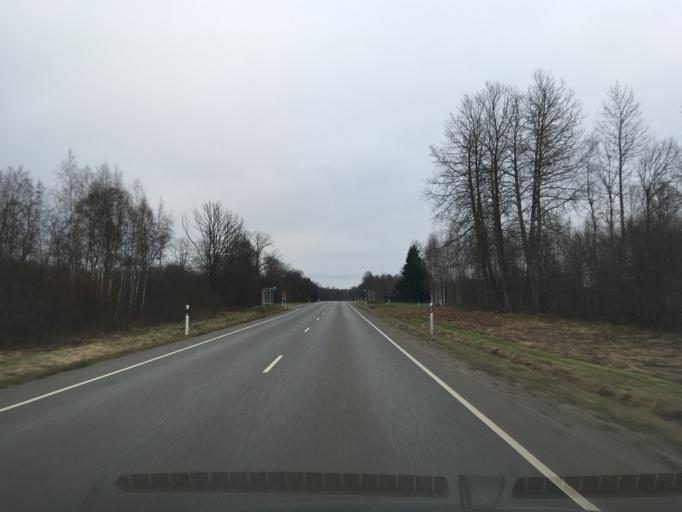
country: EE
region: Laeaene-Virumaa
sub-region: Kadrina vald
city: Kadrina
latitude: 59.4508
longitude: 26.0436
